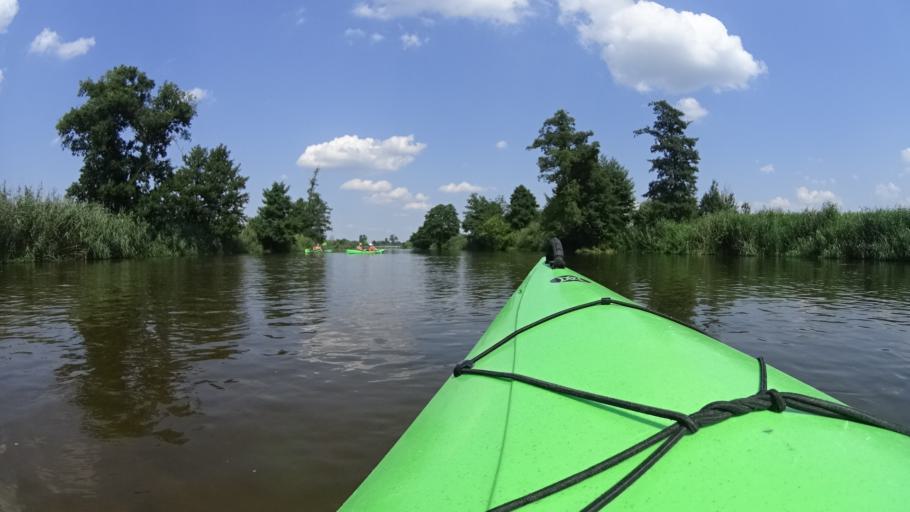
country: PL
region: Masovian Voivodeship
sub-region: Powiat bialobrzeski
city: Wysmierzyce
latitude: 51.6499
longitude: 20.8194
